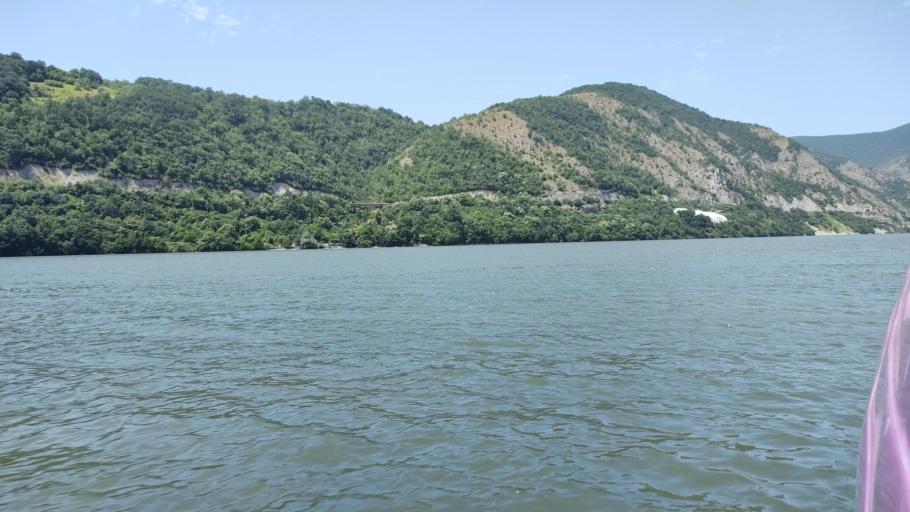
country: RO
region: Mehedinti
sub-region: Comuna Svinita
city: Svinita
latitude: 44.5505
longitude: 22.0352
